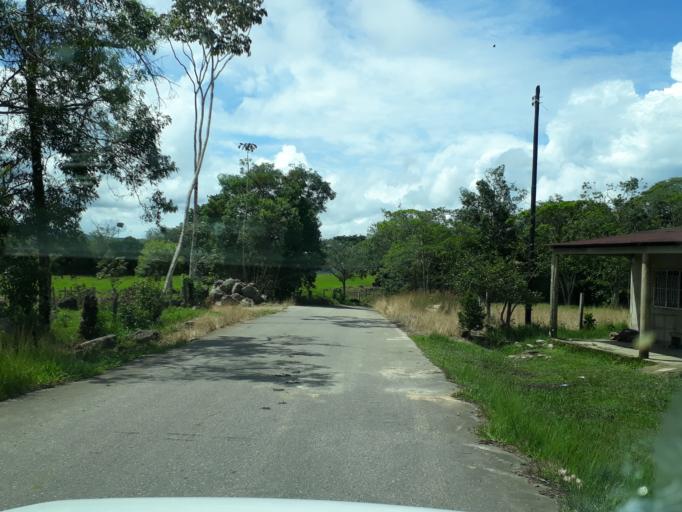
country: CO
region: Cundinamarca
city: Medina
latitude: 4.6397
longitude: -73.3105
